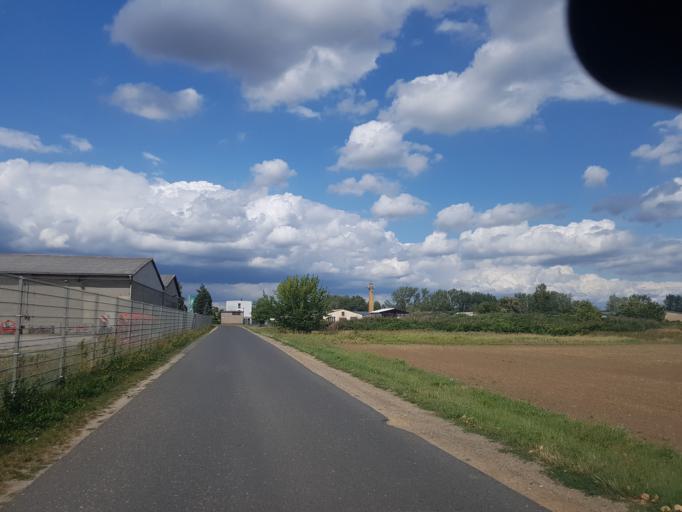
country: DE
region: Brandenburg
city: Herzberg
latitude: 51.6793
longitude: 13.2390
